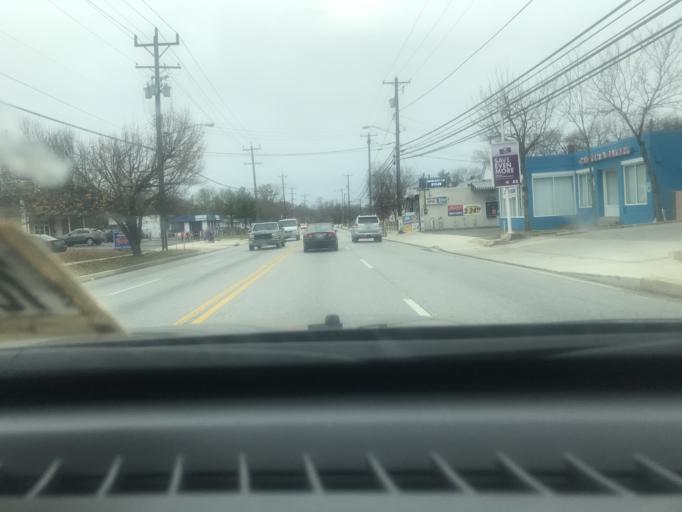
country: US
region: Maryland
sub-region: Prince George's County
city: Temple Hills
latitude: 38.7875
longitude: -76.9386
